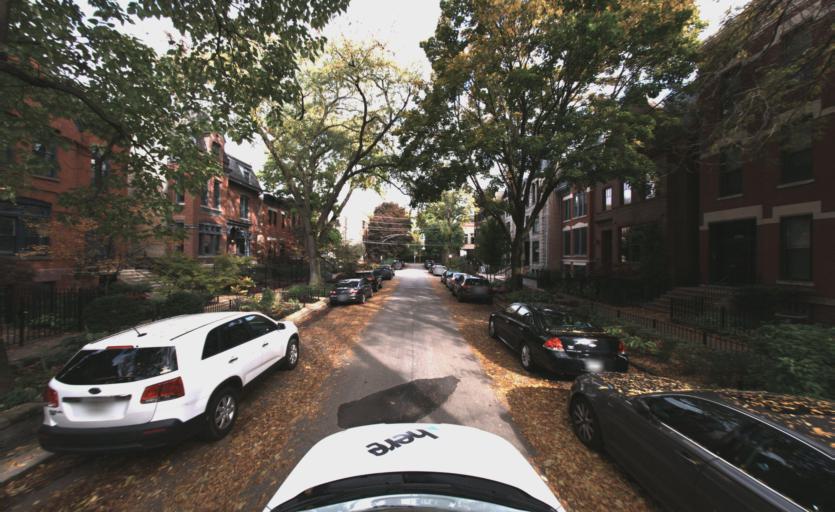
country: US
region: Illinois
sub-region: Cook County
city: Chicago
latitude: 41.9227
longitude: -87.6499
